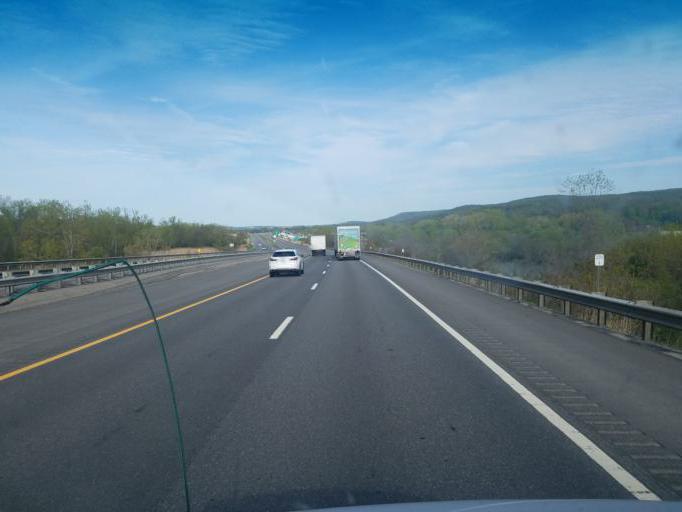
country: US
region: New York
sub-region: Herkimer County
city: Mohawk
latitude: 43.0173
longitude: -75.0072
